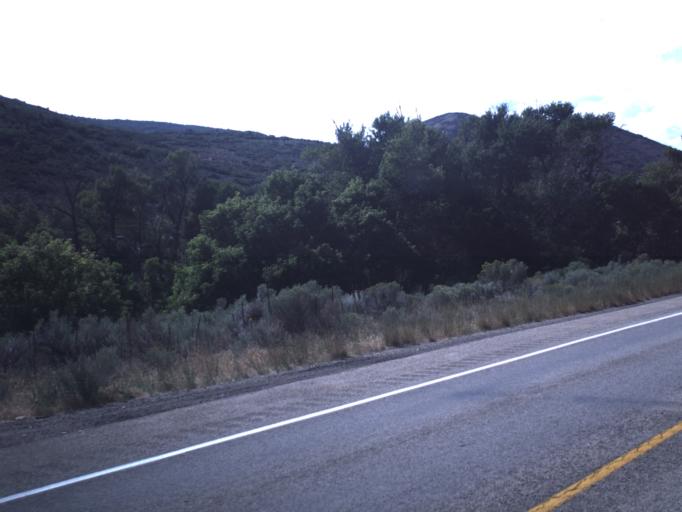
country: US
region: Utah
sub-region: Wasatch County
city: Heber
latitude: 40.4330
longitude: -111.3537
